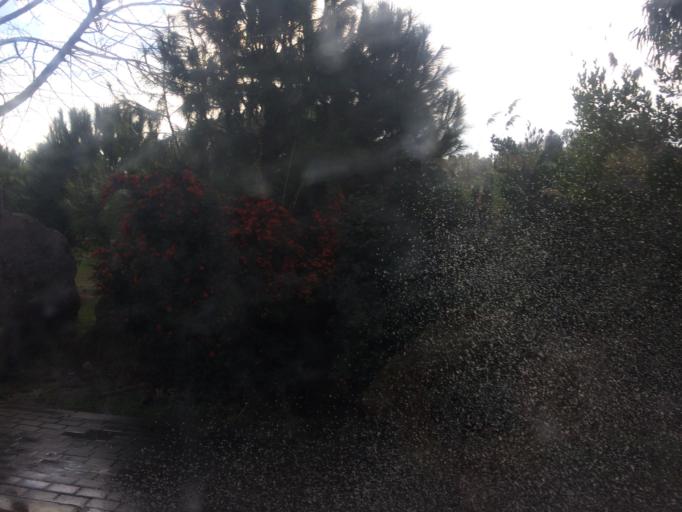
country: TR
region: Izmir
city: Karsiyaka
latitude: 38.4891
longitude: 26.9580
